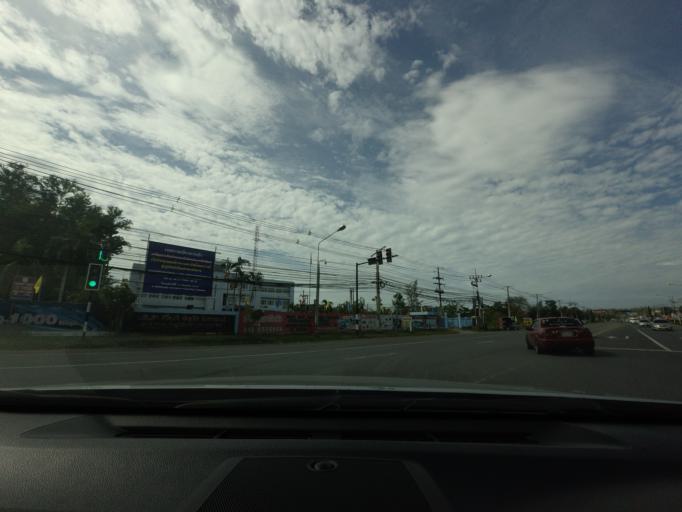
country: TH
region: Songkhla
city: Khlong Hoi Khong
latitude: 6.9488
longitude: 100.4134
